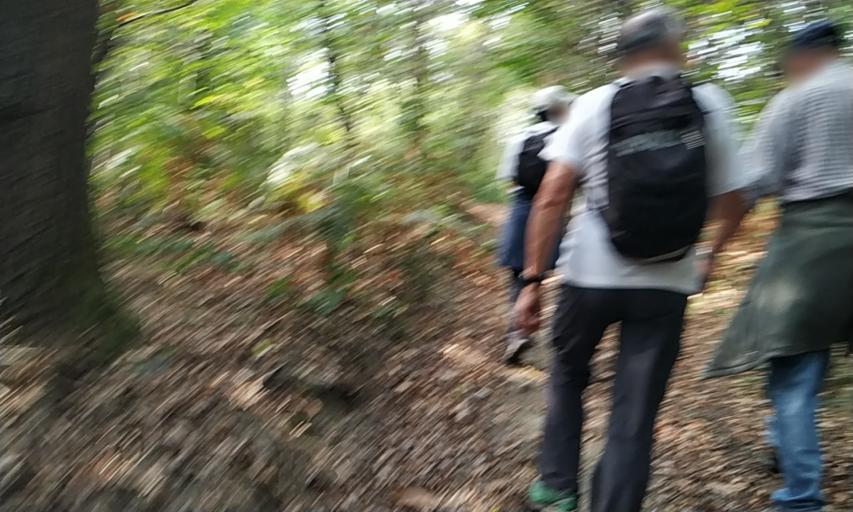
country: IT
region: Piedmont
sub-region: Provincia di Biella
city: Dorzano
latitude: 45.4346
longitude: 8.0825
